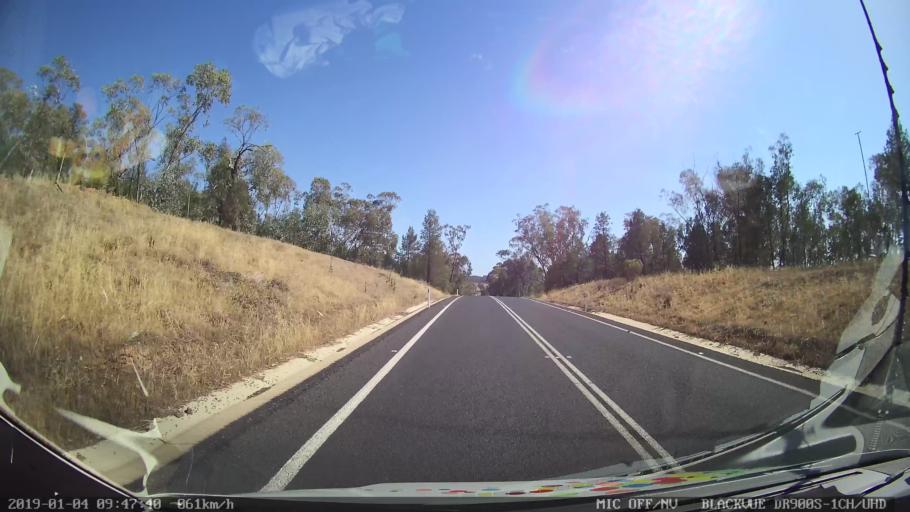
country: AU
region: New South Wales
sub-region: Cabonne
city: Canowindra
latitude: -33.6042
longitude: 148.4314
